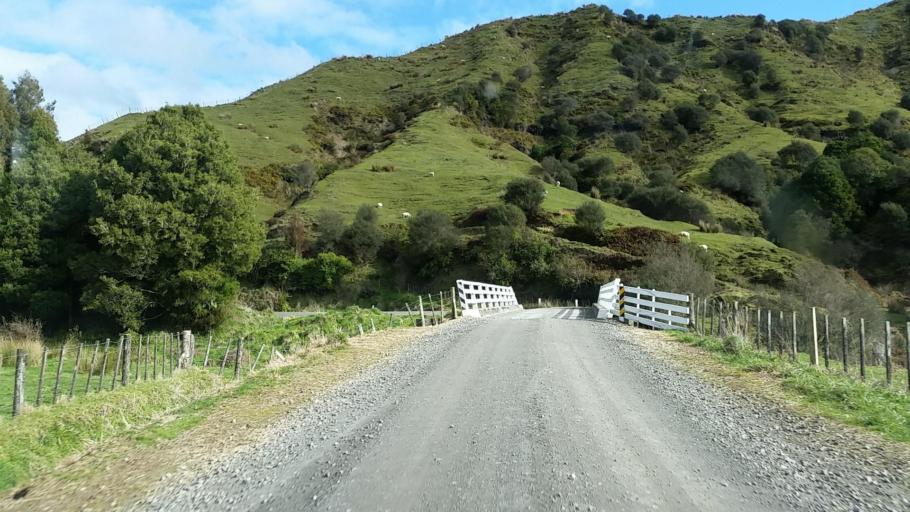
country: NZ
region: Taranaki
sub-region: New Plymouth District
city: Waitara
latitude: -39.1482
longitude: 174.5604
